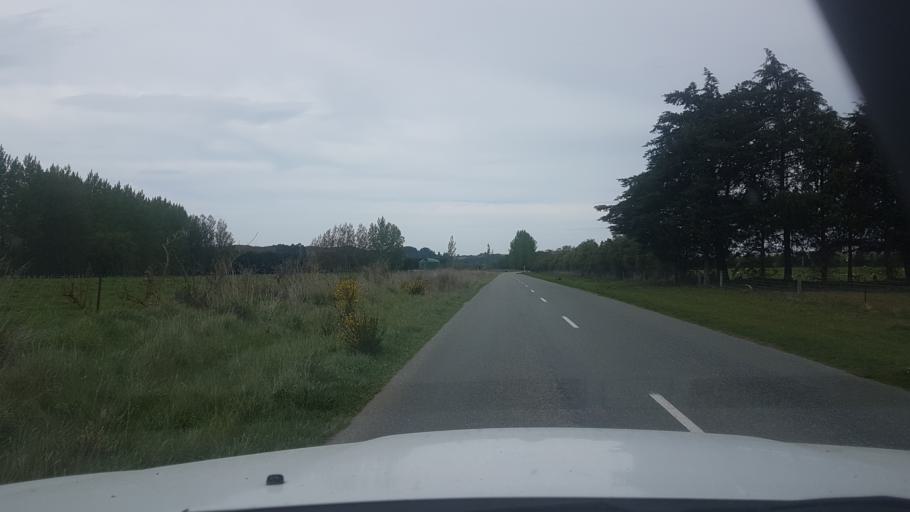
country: NZ
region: Canterbury
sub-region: Timaru District
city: Pleasant Point
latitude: -44.0735
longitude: 171.1674
